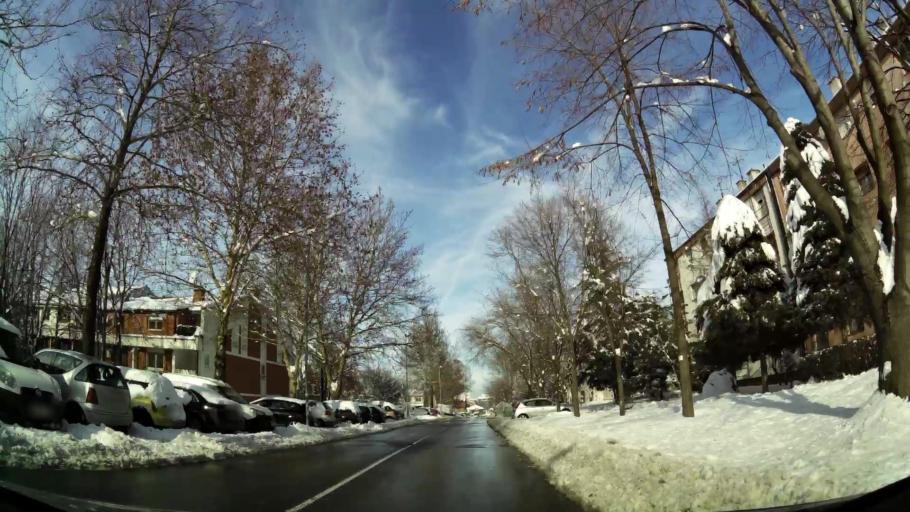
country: RS
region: Central Serbia
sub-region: Belgrade
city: Zvezdara
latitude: 44.7941
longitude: 20.5362
